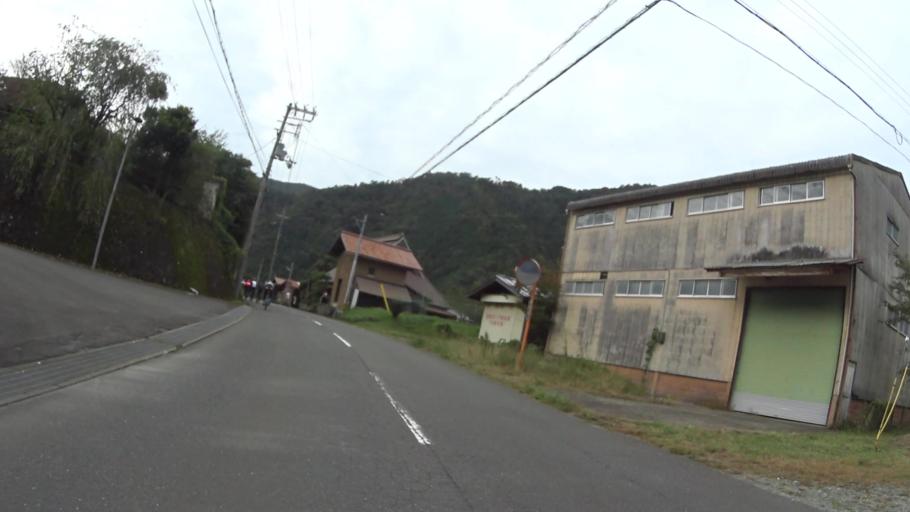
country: JP
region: Fukui
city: Obama
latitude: 35.2981
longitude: 135.6070
